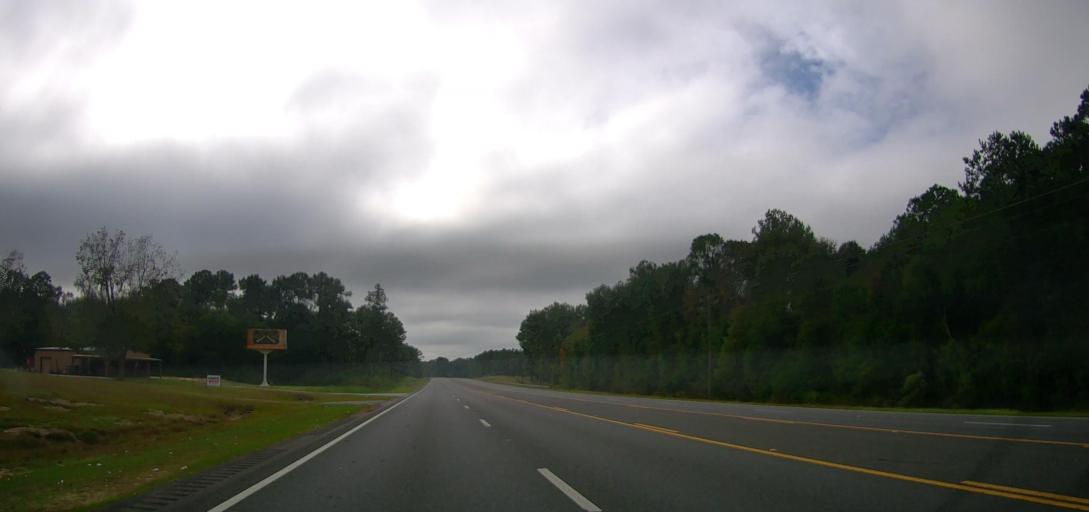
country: US
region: Georgia
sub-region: Thomas County
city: Thomasville
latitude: 30.9820
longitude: -83.8821
